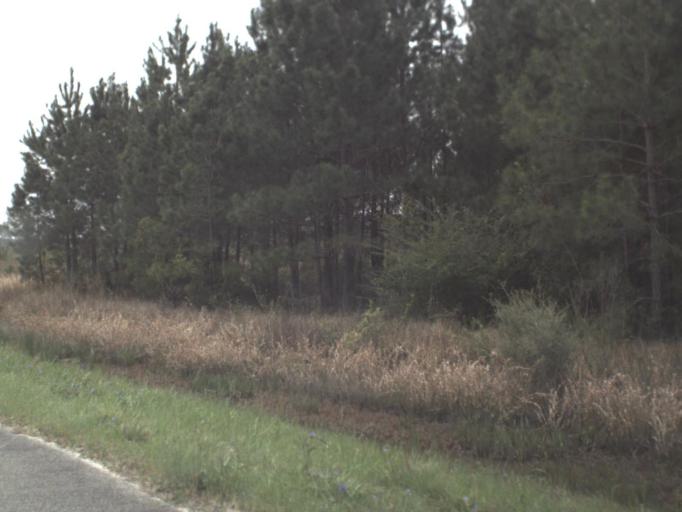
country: US
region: Florida
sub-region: Gulf County
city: Wewahitchka
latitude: 29.9873
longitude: -85.1686
